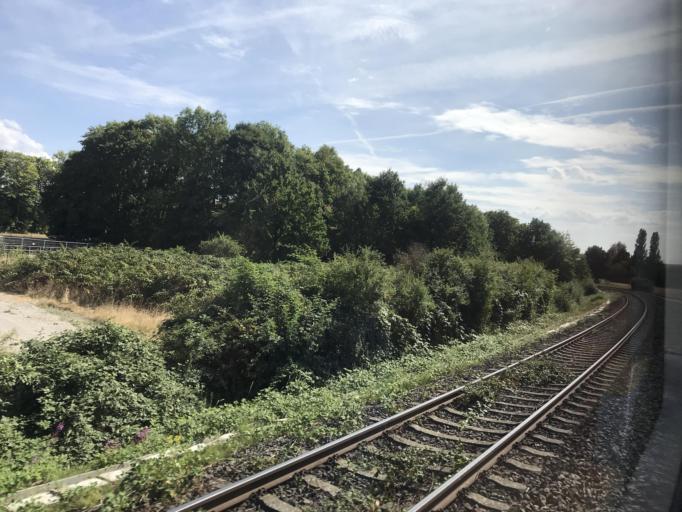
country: DE
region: Hesse
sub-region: Regierungsbezirk Giessen
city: Limburg an der Lahn
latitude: 50.3849
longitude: 8.0374
